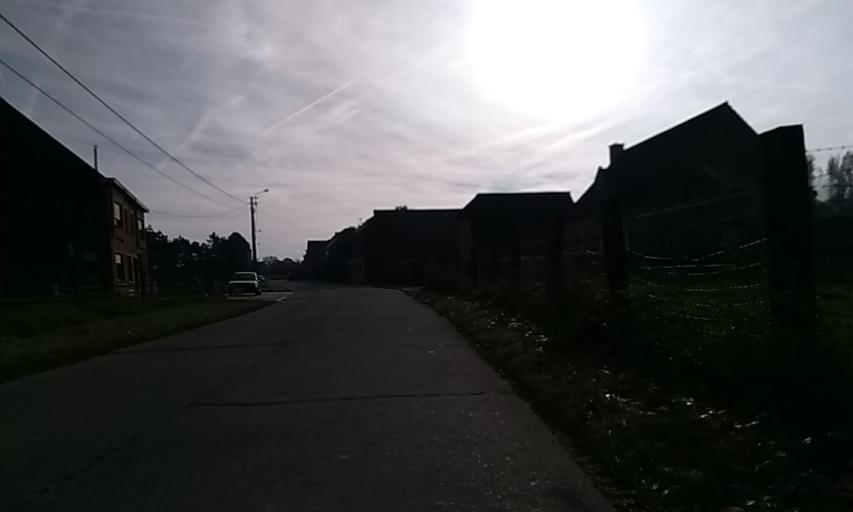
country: BE
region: Flanders
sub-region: Provincie Oost-Vlaanderen
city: Sint-Lievens-Houtem
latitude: 50.9257
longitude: 3.8345
